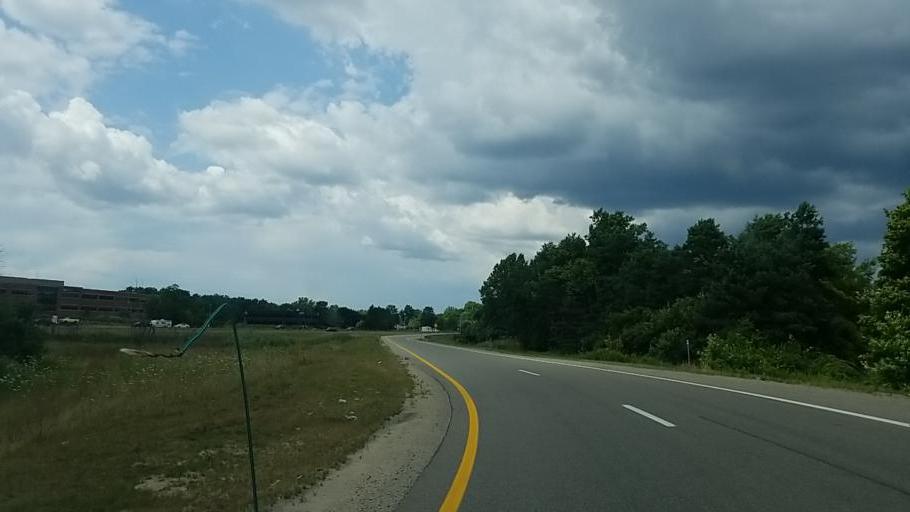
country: US
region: Michigan
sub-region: Kent County
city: East Grand Rapids
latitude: 42.9483
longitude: -85.5650
